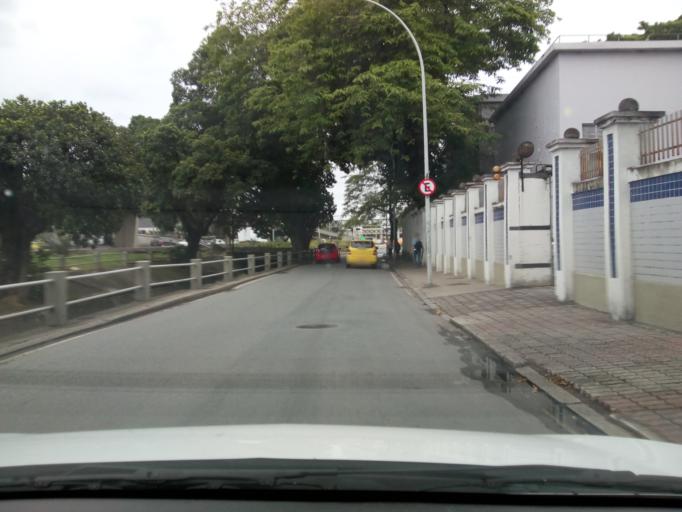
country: BR
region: Rio de Janeiro
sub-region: Rio De Janeiro
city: Rio de Janeiro
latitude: -22.9115
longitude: -43.2248
